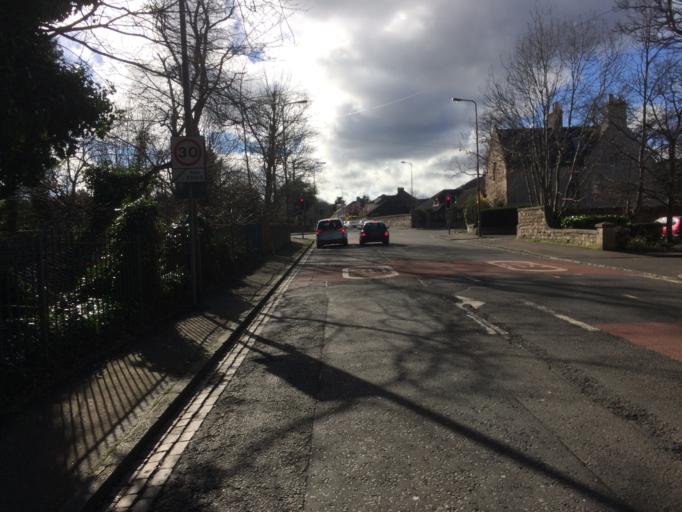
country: GB
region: Scotland
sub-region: West Lothian
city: Seafield
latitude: 55.9458
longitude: -3.1343
